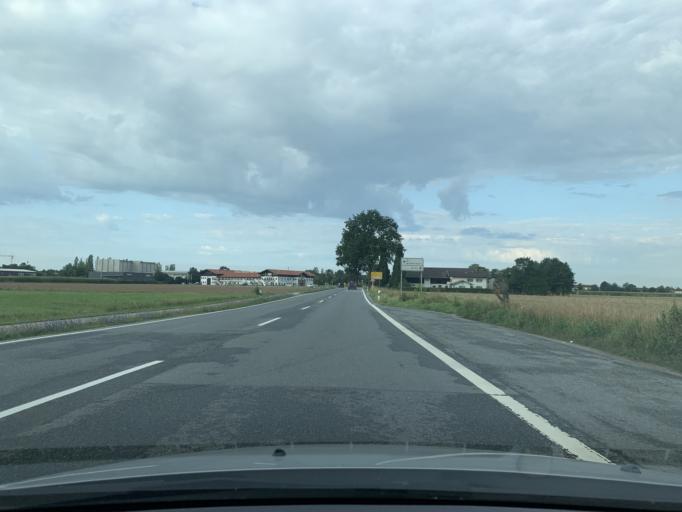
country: DE
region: Bavaria
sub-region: Upper Bavaria
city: Rohrbach
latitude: 48.2647
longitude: 12.5456
